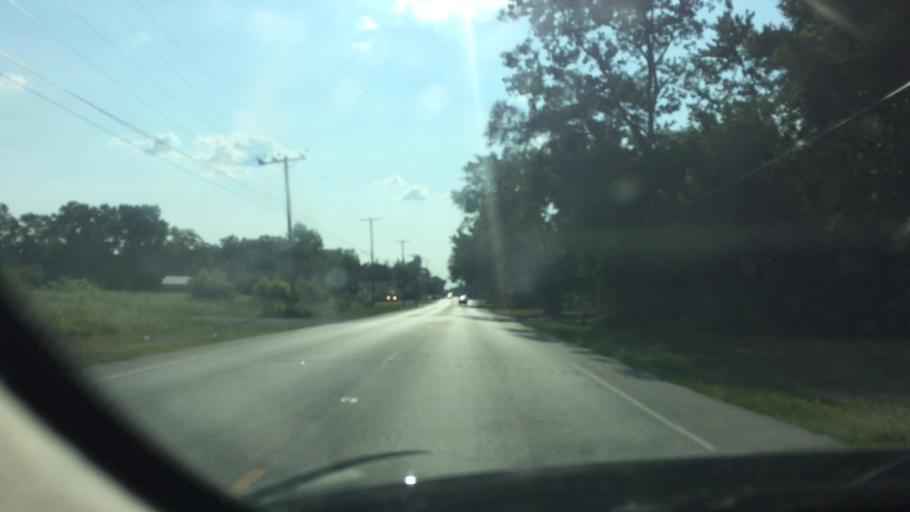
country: US
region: Ohio
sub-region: Lucas County
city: Holland
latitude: 41.6540
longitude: -83.6990
